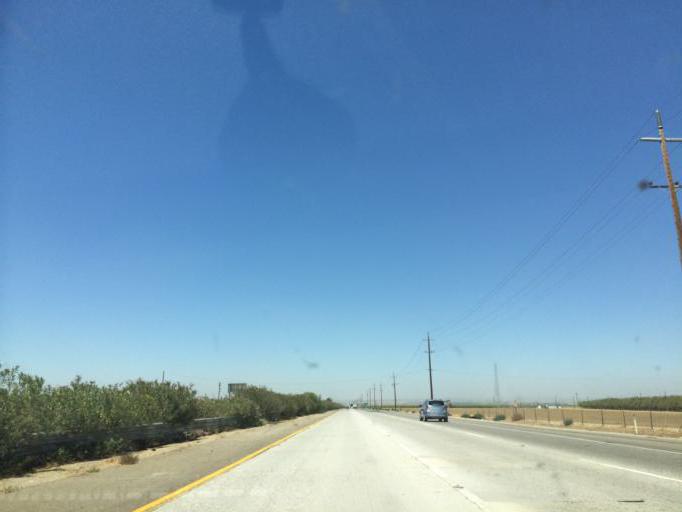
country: US
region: California
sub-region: Kern County
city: Frazier Park
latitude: 35.0285
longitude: -118.9586
